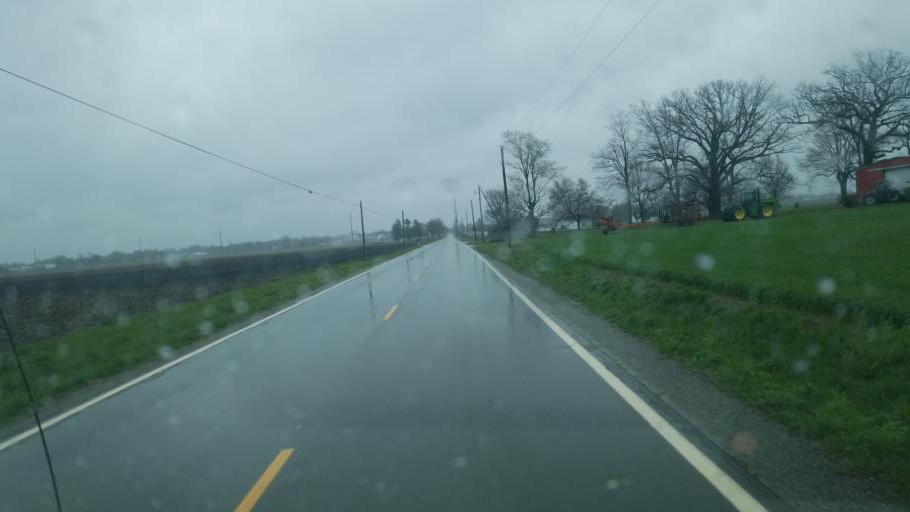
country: US
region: Ohio
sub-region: Wyandot County
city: Upper Sandusky
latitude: 40.8180
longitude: -83.3095
